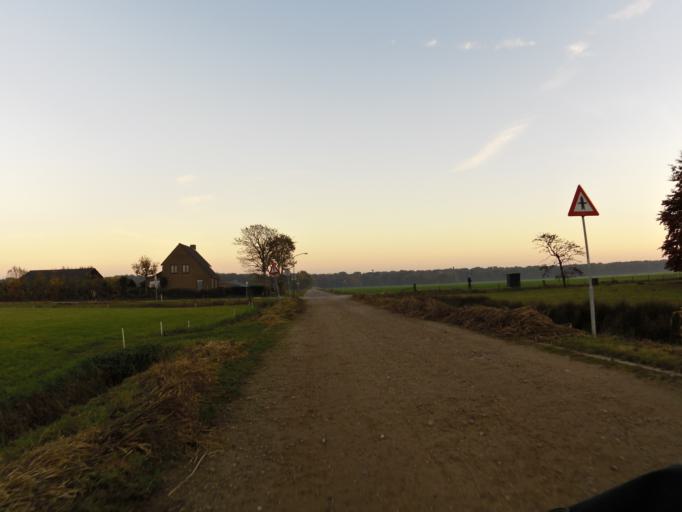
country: NL
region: North Brabant
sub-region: Gemeente Vught
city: Vught
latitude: 51.6762
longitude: 5.2765
